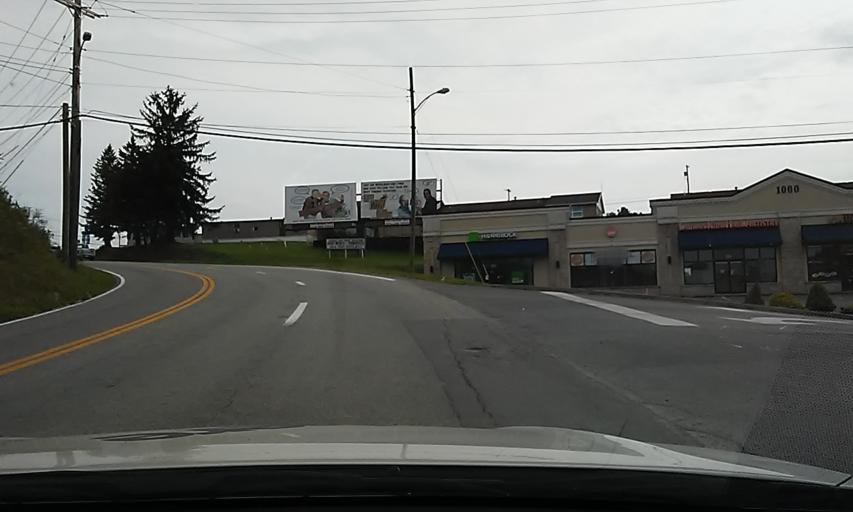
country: US
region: West Virginia
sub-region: Monongalia County
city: Morgantown
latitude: 39.6514
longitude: -79.9210
